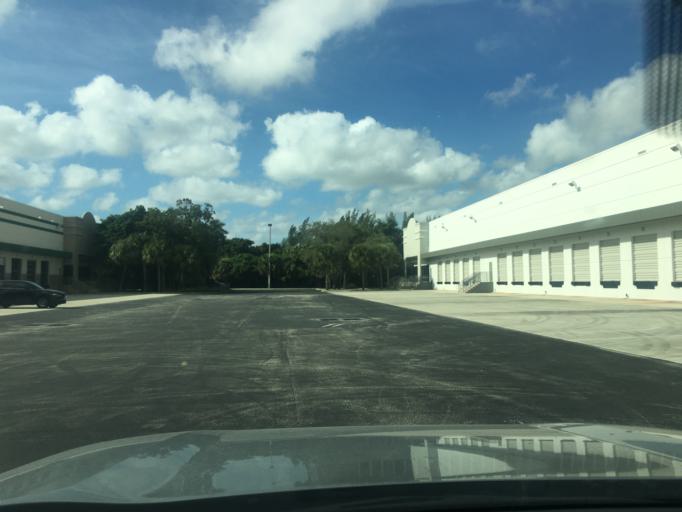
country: US
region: Florida
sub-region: Broward County
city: Broadview Park
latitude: 26.0742
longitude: -80.1829
